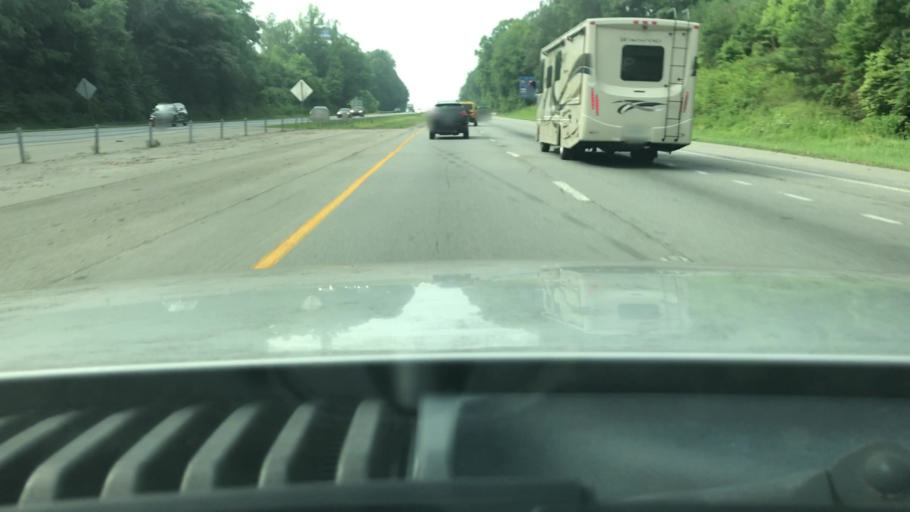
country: US
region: North Carolina
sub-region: Yadkin County
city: Jonesville
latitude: 36.2475
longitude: -80.8203
